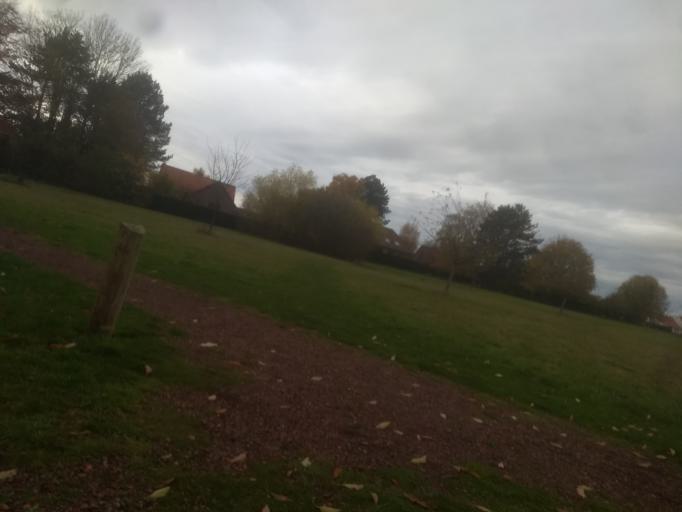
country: FR
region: Nord-Pas-de-Calais
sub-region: Departement du Pas-de-Calais
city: Dainville
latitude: 50.2846
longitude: 2.7257
